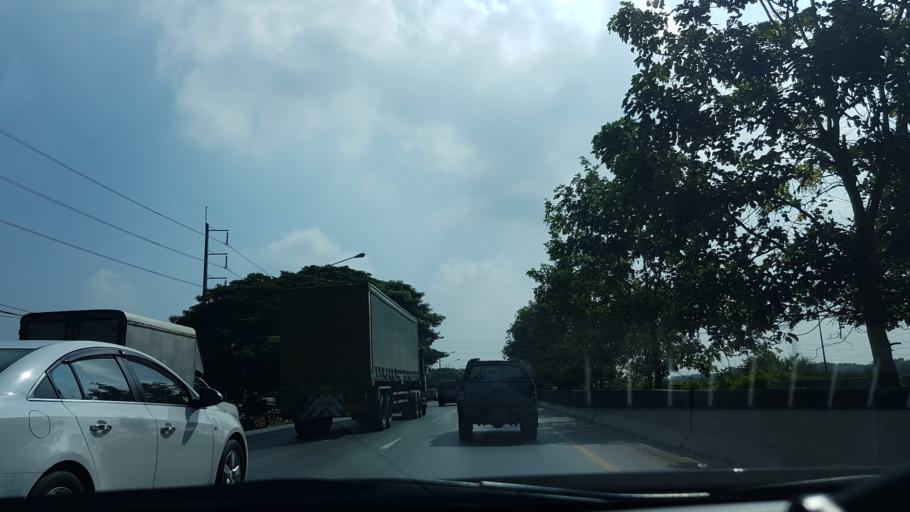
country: TH
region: Phra Nakhon Si Ayutthaya
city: Bang Pa-in
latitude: 14.1697
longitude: 100.6064
